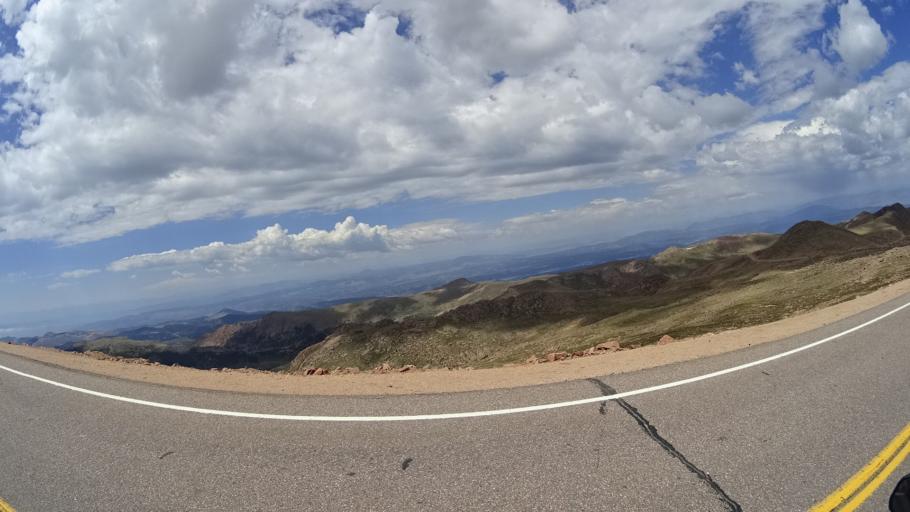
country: US
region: Colorado
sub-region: El Paso County
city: Cascade-Chipita Park
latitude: 38.8415
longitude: -105.0494
